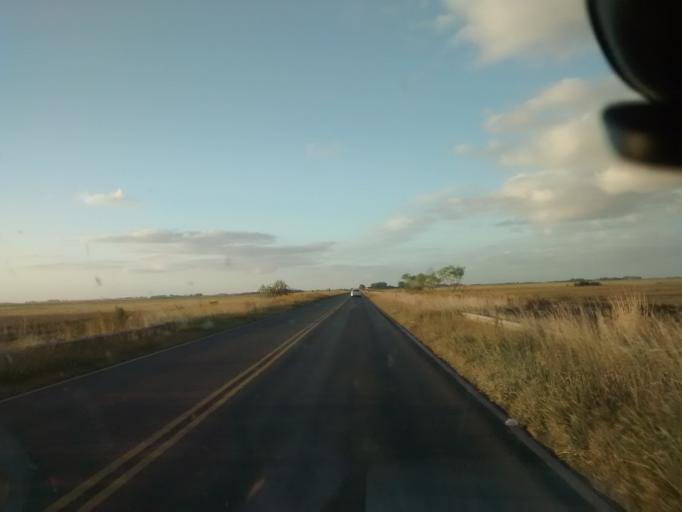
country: AR
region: Buenos Aires
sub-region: Partido de General Belgrano
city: General Belgrano
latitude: -35.6987
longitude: -58.4799
